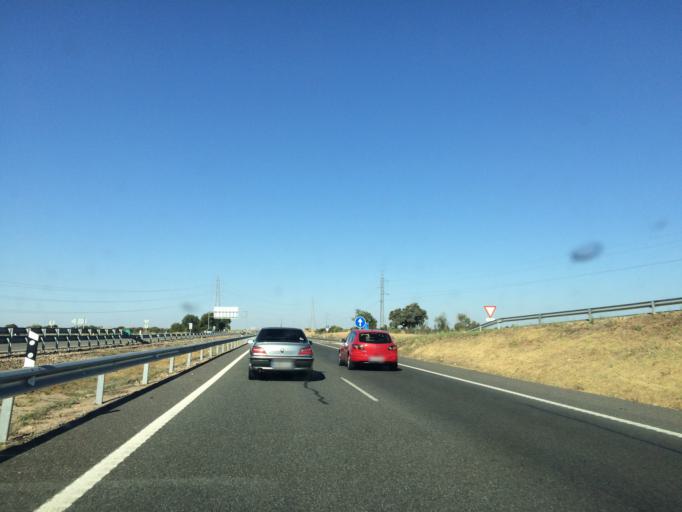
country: ES
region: Castille-La Mancha
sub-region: Province of Toledo
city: Velada
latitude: 39.9367
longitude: -4.9804
